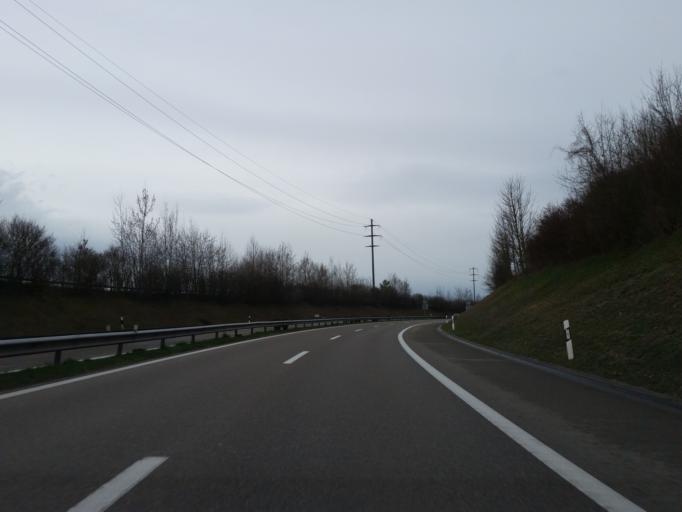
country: CH
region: Thurgau
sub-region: Kreuzlingen District
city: Tagerwilen
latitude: 47.6274
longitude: 9.1411
